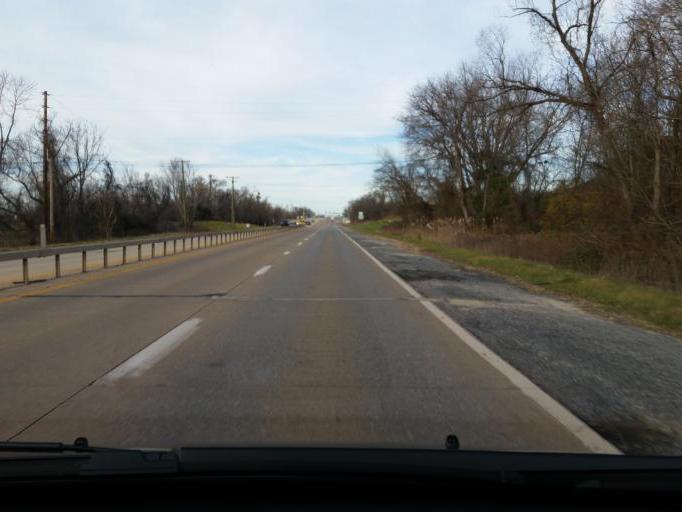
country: US
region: Pennsylvania
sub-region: Dauphin County
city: Middletown
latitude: 40.2176
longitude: -76.7189
